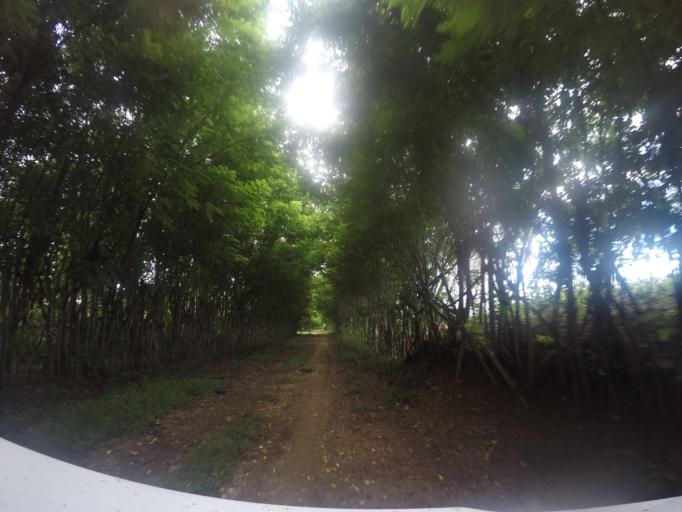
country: TL
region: Lautem
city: Lospalos
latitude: -8.5067
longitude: 127.0152
